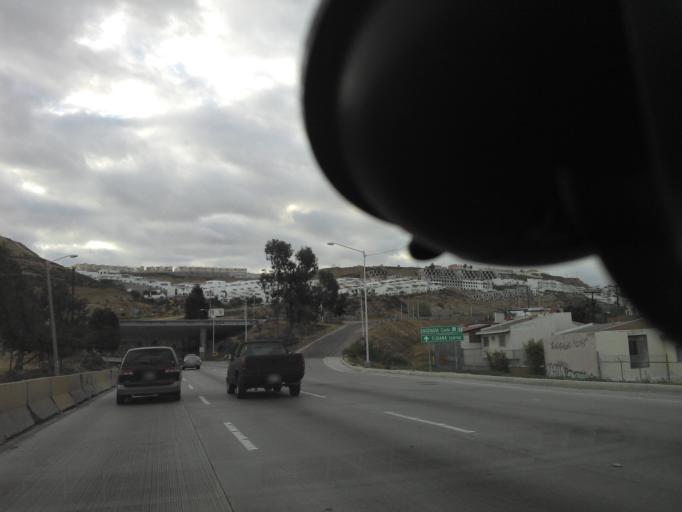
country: US
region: California
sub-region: San Diego County
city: Imperial Beach
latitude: 32.5338
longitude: -117.1099
